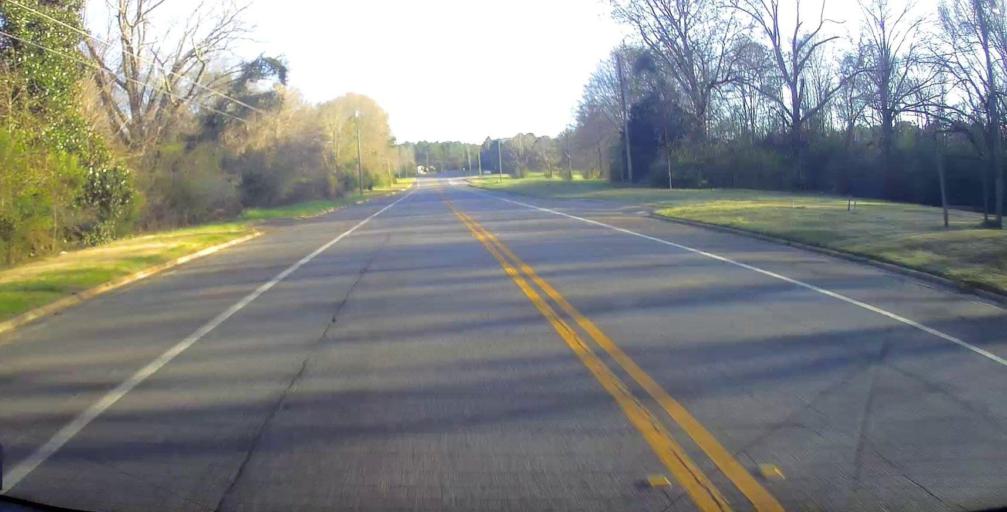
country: US
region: Georgia
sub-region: Talbot County
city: Talbotton
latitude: 32.6613
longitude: -84.5335
